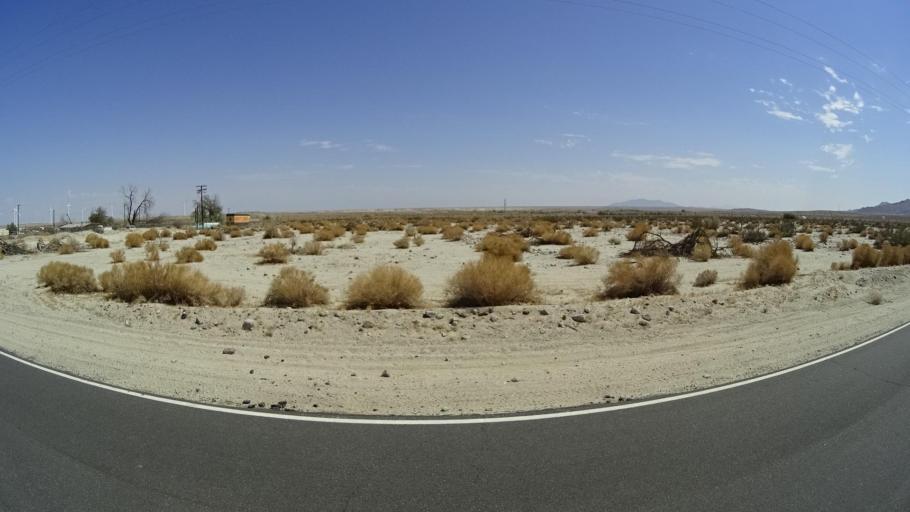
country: US
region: California
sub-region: Imperial County
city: Seeley
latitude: 32.7436
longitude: -115.9942
